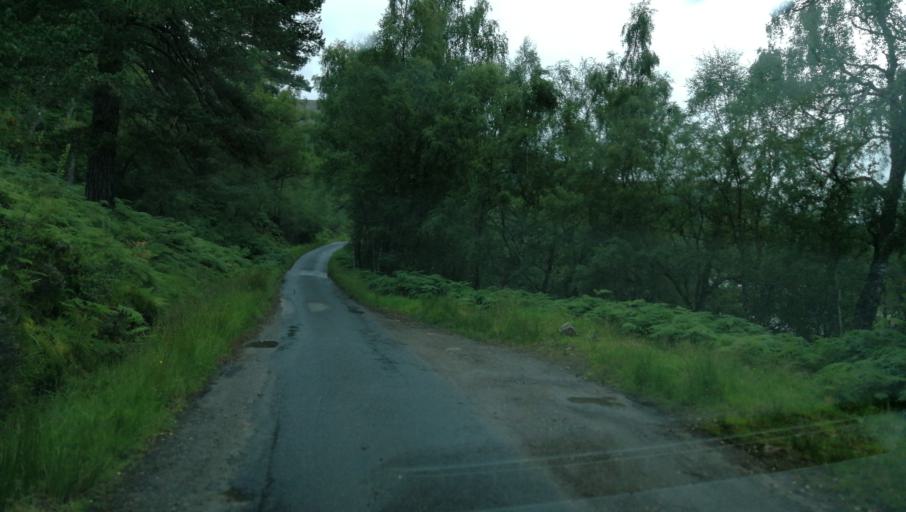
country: GB
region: Scotland
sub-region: Highland
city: Spean Bridge
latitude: 57.2885
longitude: -4.9193
